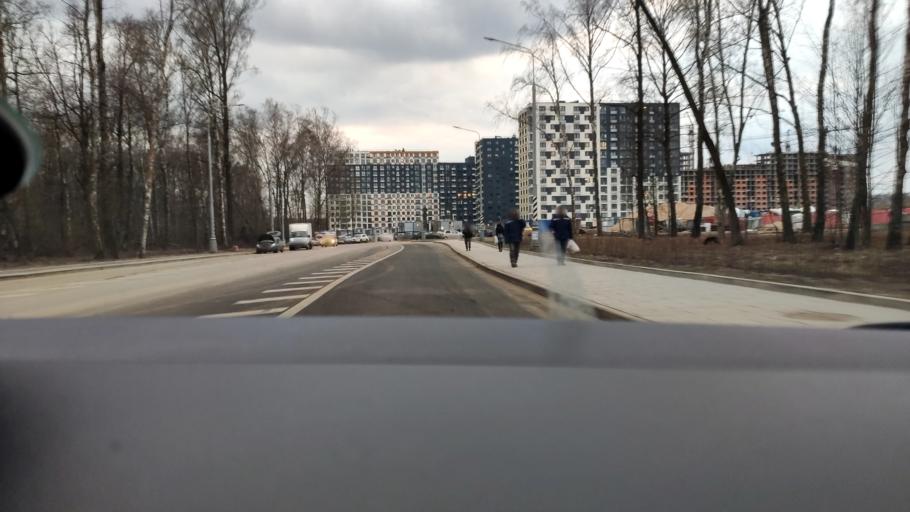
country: RU
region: Moskovskaya
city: Kommunarka
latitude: 55.5561
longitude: 37.4715
